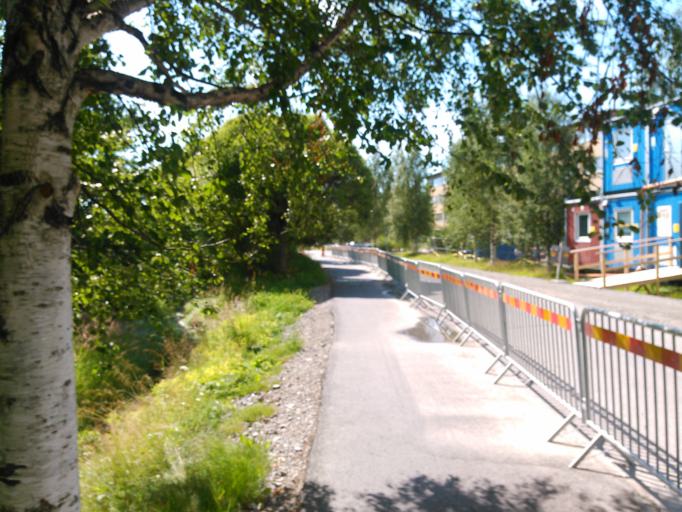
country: SE
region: Vaesterbotten
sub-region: Umea Kommun
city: Umea
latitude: 63.8241
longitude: 20.3097
